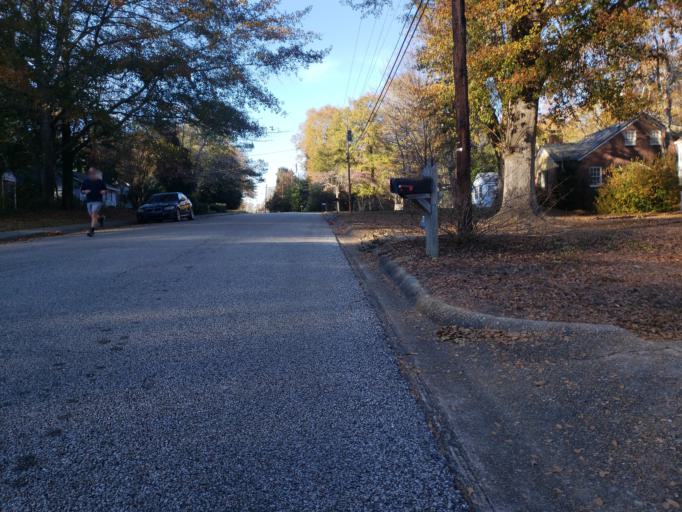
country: US
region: Alabama
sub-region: Lee County
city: Auburn
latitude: 32.5945
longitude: -85.4738
